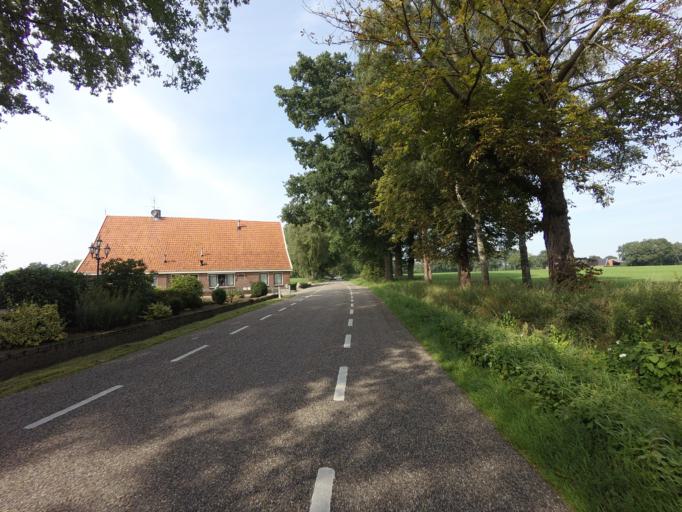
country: NL
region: Overijssel
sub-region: Gemeente Tubbergen
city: Tubbergen
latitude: 52.4208
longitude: 6.7763
